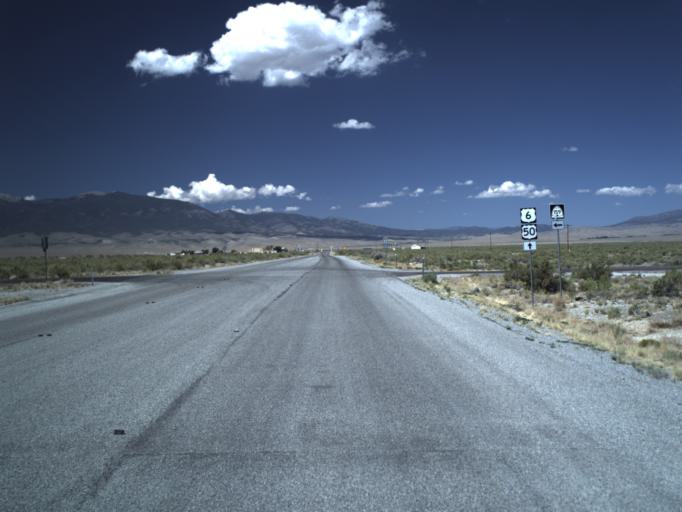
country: US
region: Nevada
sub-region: White Pine County
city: McGill
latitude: 39.0561
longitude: -114.0358
